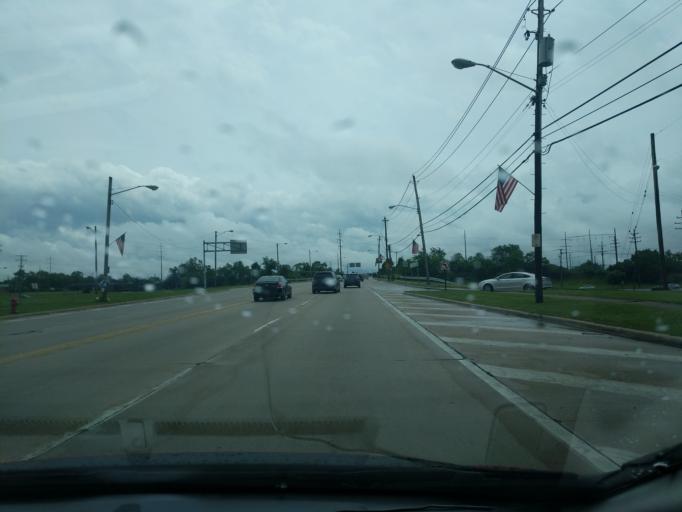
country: US
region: Ohio
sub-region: Cuyahoga County
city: Warrensville Heights
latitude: 41.4312
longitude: -81.5361
